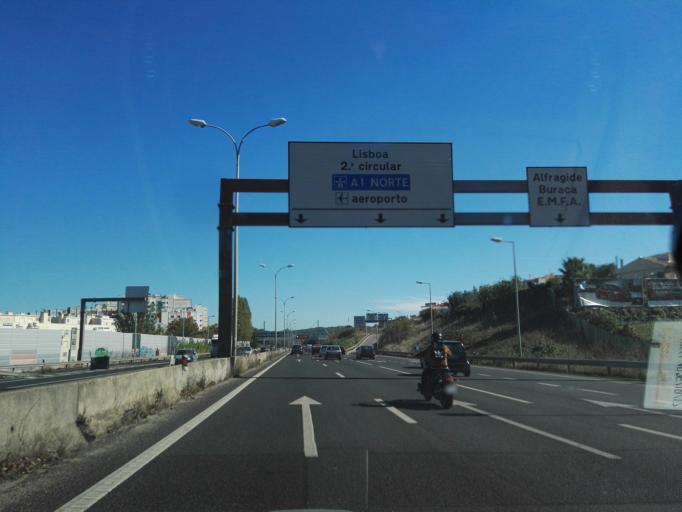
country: PT
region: Lisbon
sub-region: Amadora
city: Amadora
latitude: 38.7414
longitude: -9.2226
